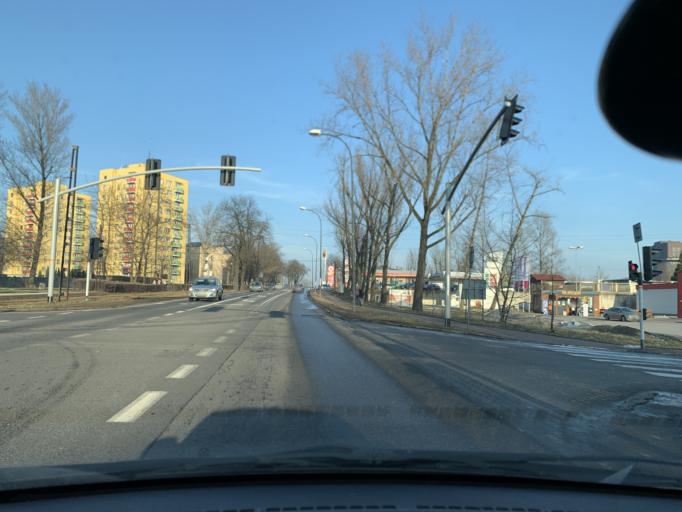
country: PL
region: Silesian Voivodeship
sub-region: Bytom
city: Bytom
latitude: 50.3390
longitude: 18.9039
